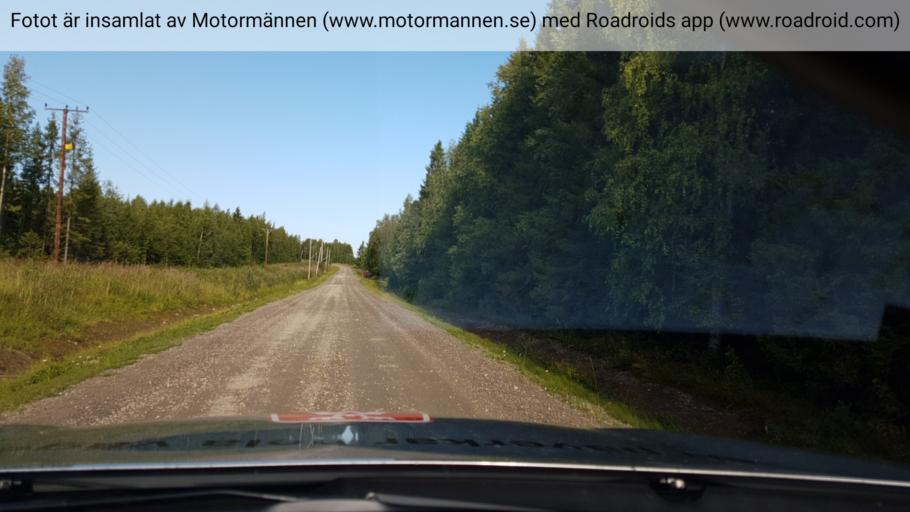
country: SE
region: Norrbotten
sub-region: Kalix Kommun
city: Kalix
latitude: 66.1129
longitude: 23.2818
